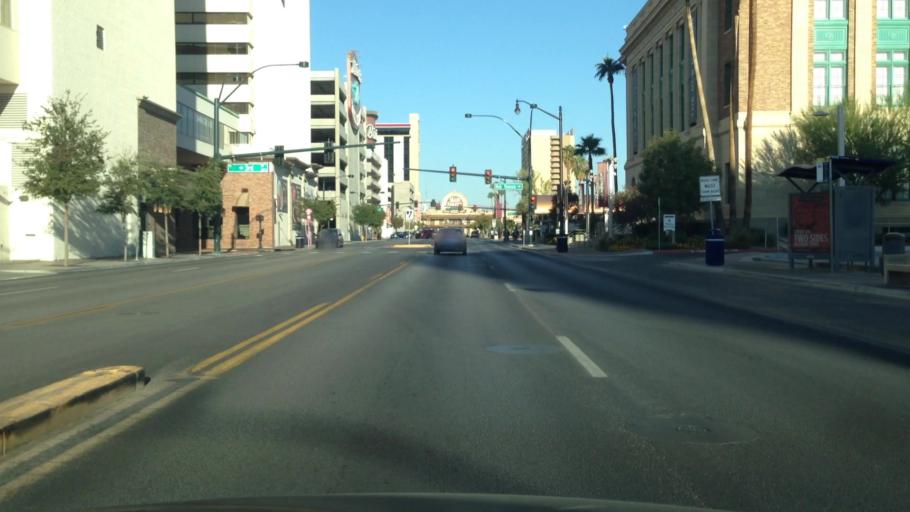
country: US
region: Nevada
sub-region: Clark County
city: Las Vegas
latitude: 36.1722
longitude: -115.1406
